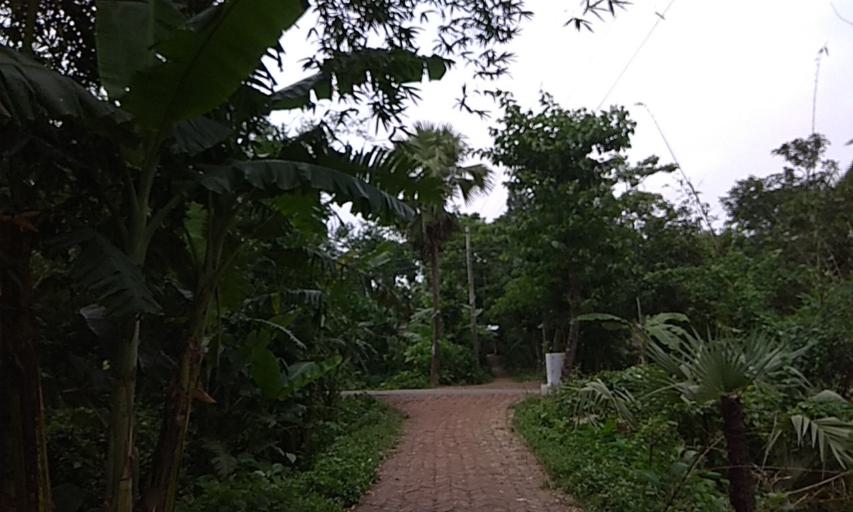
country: BD
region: Dhaka
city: Dohar
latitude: 23.5430
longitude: 89.9924
